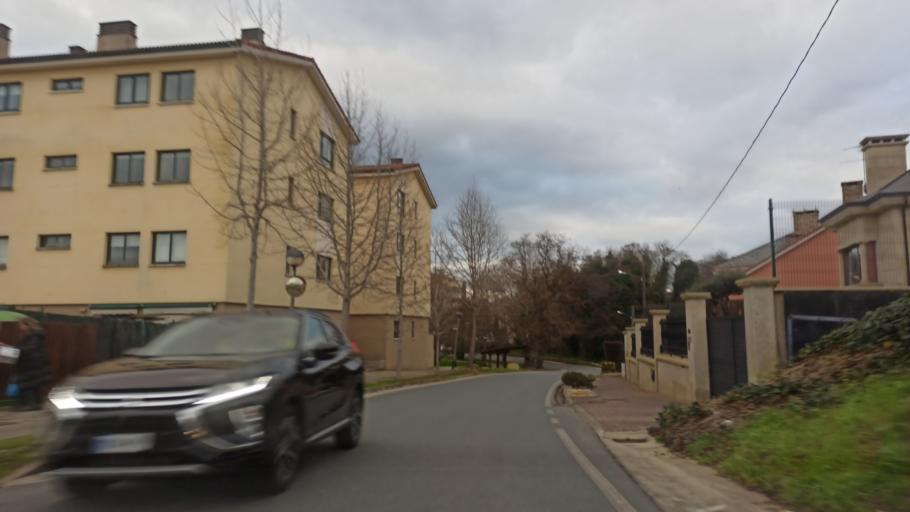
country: ES
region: Galicia
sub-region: Provincia da Coruna
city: Oleiros
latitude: 43.3391
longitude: -8.3484
